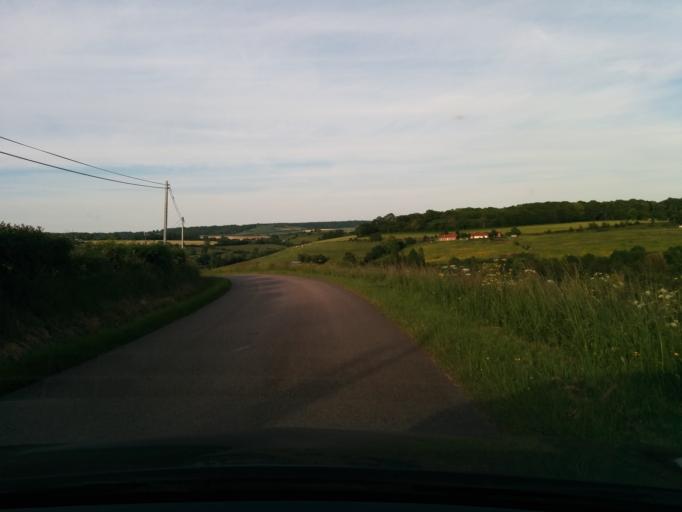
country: FR
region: Haute-Normandie
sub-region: Departement de la Seine-Maritime
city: Serqueux
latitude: 49.6860
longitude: 1.4950
